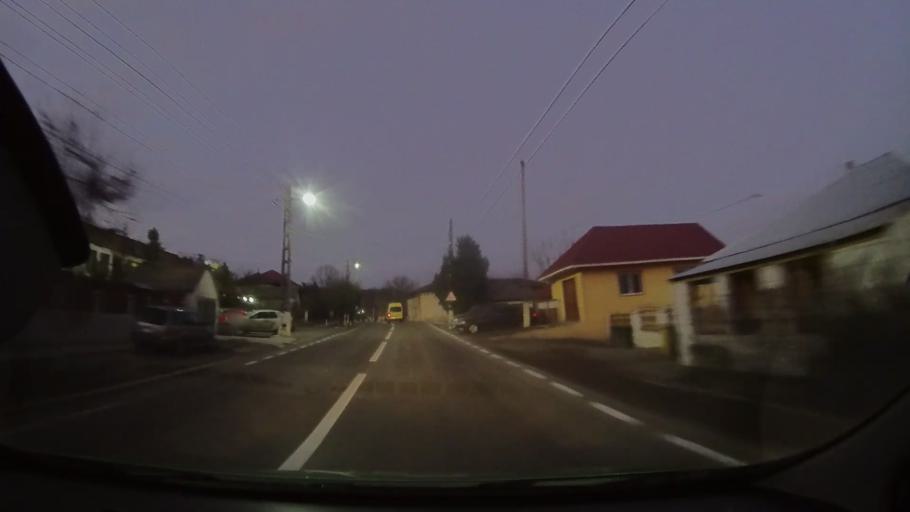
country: RO
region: Constanta
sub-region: Comuna Ion Corvin
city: Ion Corvin
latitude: 44.1116
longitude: 27.8051
